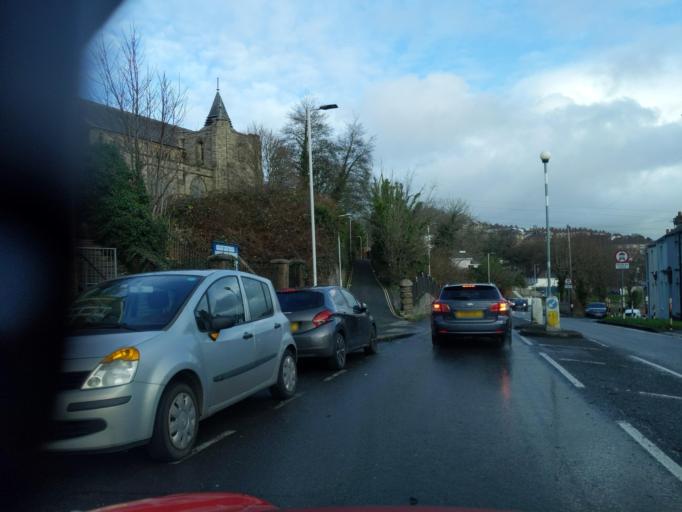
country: GB
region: England
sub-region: Plymouth
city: Plymstock
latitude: 50.3843
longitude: -4.1060
